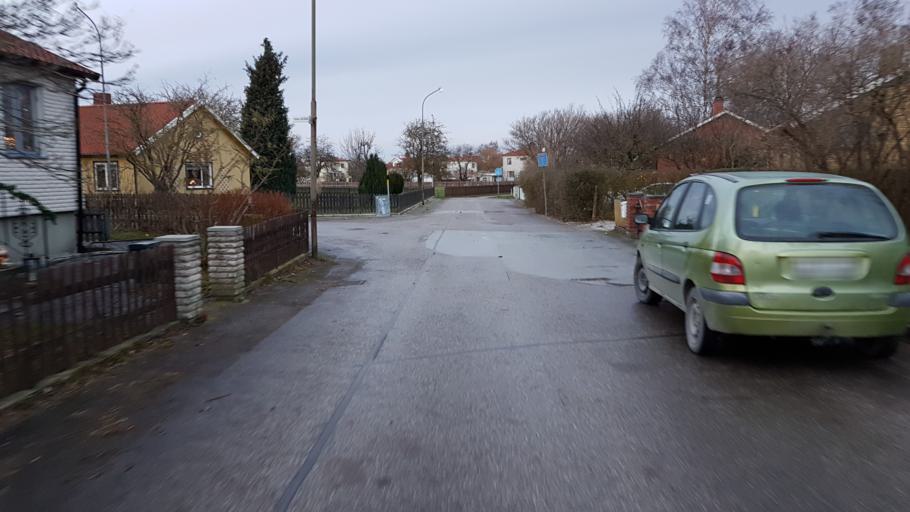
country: SE
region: Gotland
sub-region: Gotland
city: Visby
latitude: 57.6232
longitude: 18.2921
